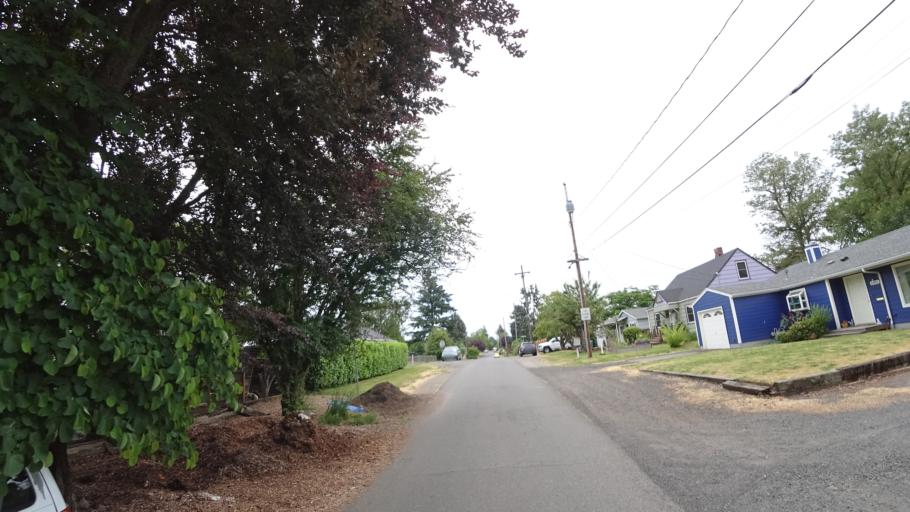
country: US
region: Oregon
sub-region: Multnomah County
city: Lents
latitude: 45.5130
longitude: -122.5722
